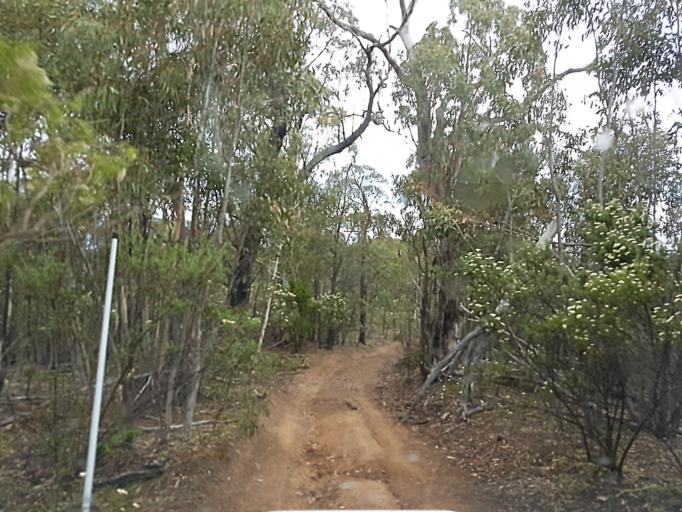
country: AU
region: New South Wales
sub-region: Snowy River
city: Jindabyne
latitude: -36.9027
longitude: 148.3425
